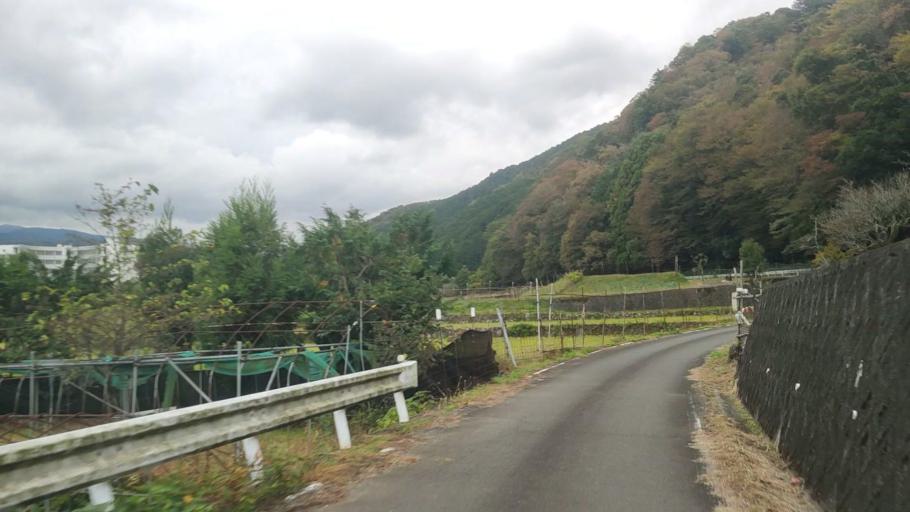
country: JP
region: Shizuoka
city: Ito
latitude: 34.9346
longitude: 138.9936
